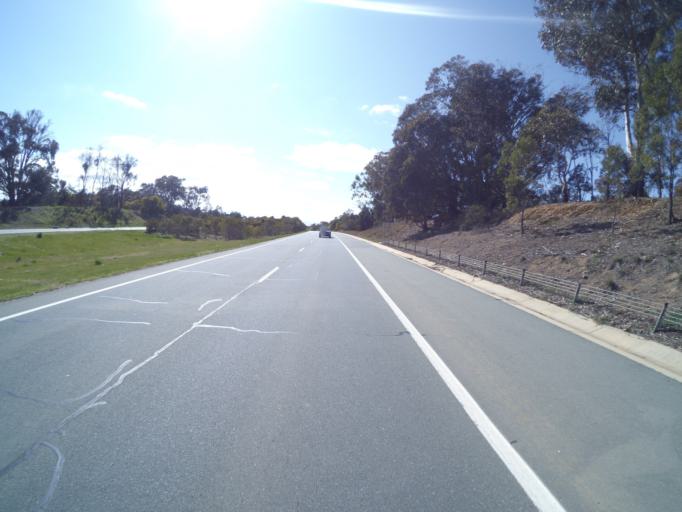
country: AU
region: Australian Capital Territory
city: Kaleen
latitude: -35.2057
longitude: 149.2005
